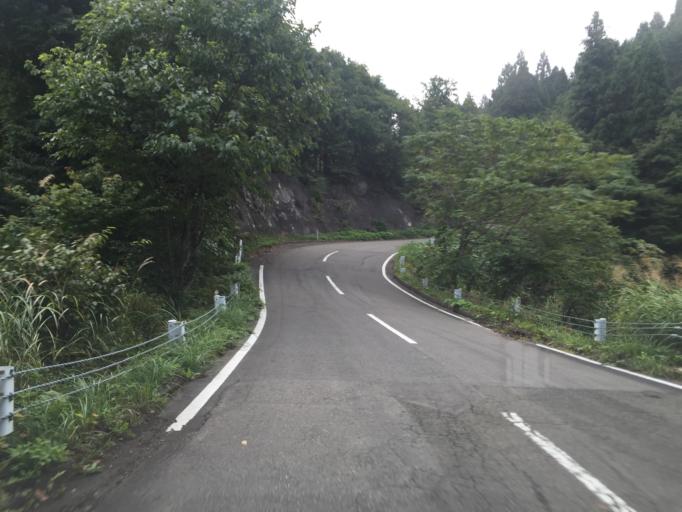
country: JP
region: Fukushima
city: Inawashiro
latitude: 37.4873
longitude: 139.9705
